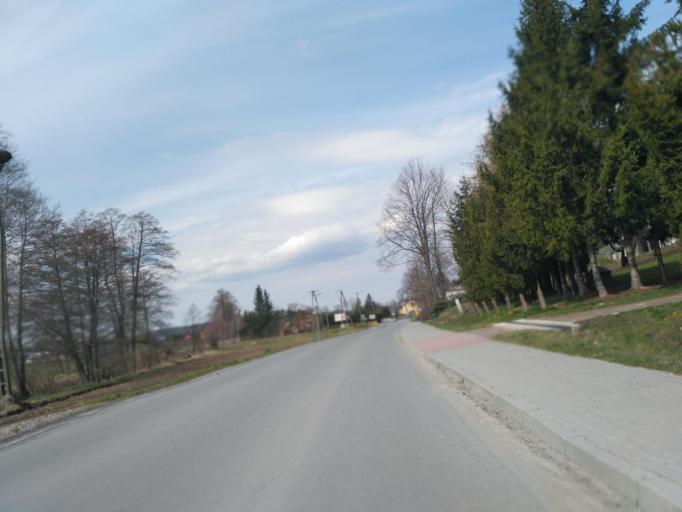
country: PL
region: Subcarpathian Voivodeship
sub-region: Powiat ropczycko-sedziszowski
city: Iwierzyce
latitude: 50.0200
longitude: 21.7897
